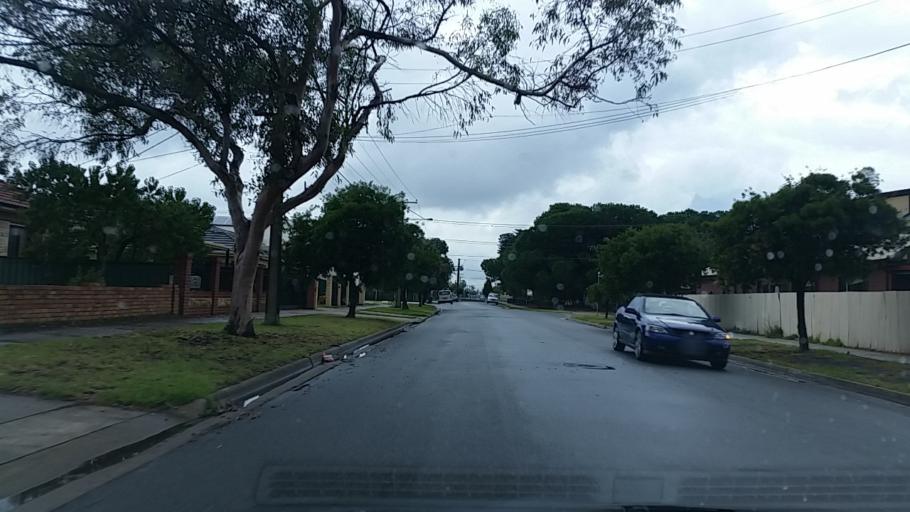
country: AU
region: South Australia
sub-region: Charles Sturt
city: Seaton
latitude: -34.8958
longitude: 138.5180
